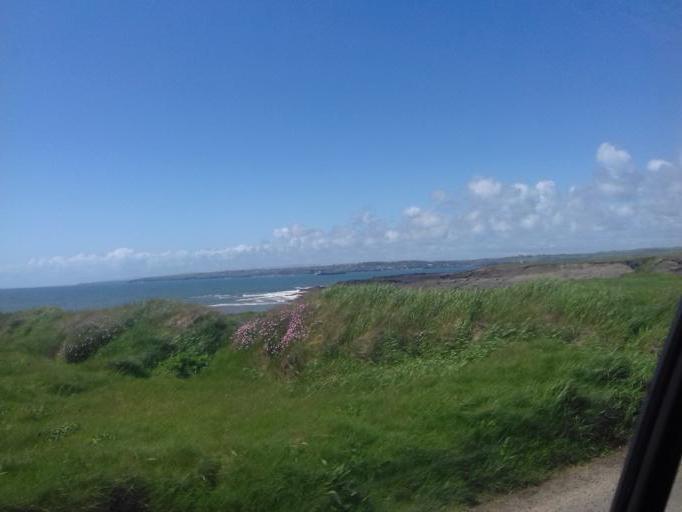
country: IE
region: Munster
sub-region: Waterford
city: Dunmore East
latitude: 52.1288
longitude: -6.9296
